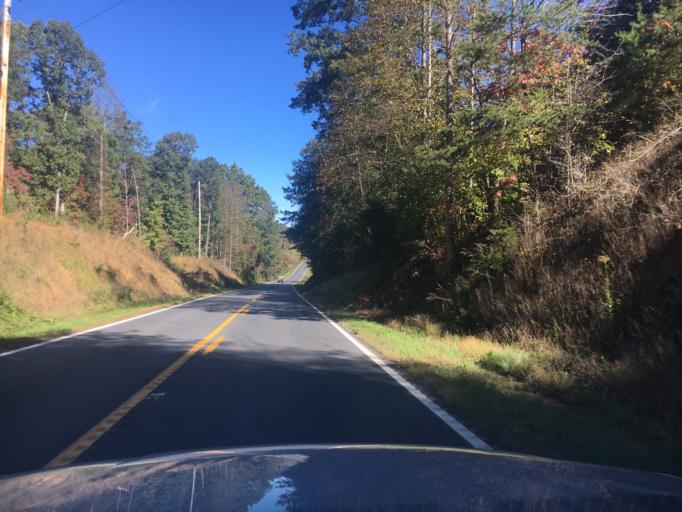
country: US
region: North Carolina
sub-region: Burke County
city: Glen Alpine
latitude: 35.6129
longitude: -81.8125
